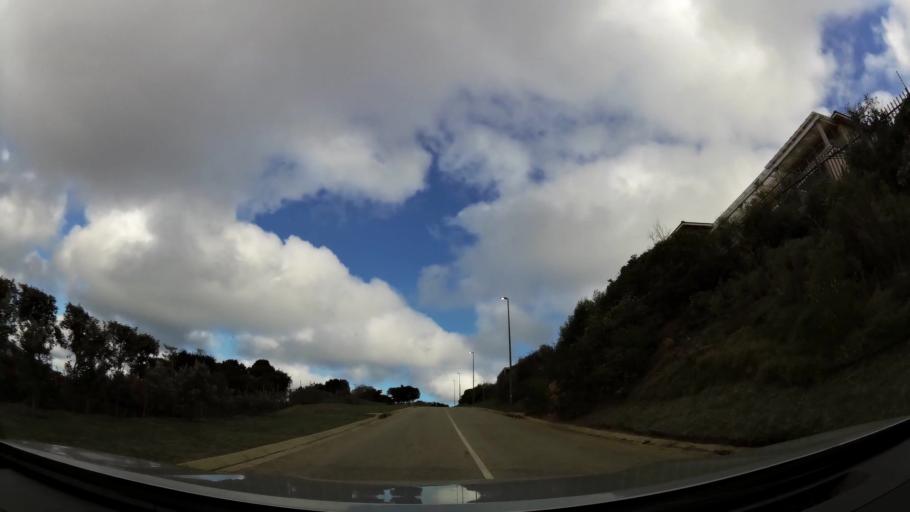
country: ZA
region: Western Cape
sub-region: Eden District Municipality
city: Plettenberg Bay
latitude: -34.0869
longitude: 23.3557
